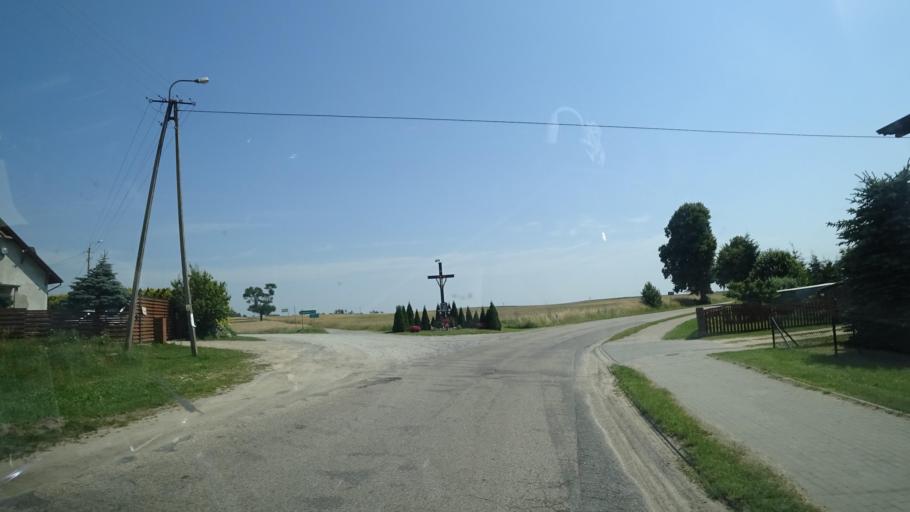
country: PL
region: Pomeranian Voivodeship
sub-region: Powiat chojnicki
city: Brusy
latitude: 53.8821
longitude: 17.6421
